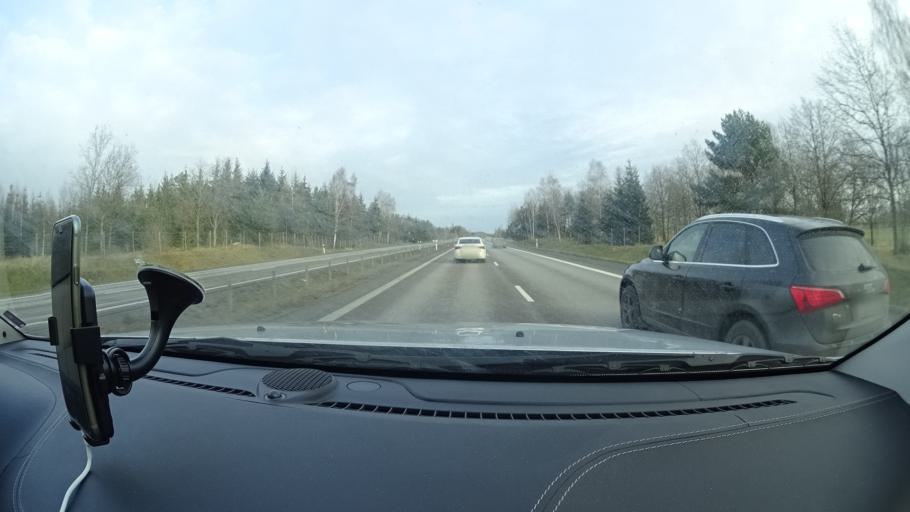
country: SE
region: OEstergoetland
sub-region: Linkopings Kommun
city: Linghem
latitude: 58.4630
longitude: 15.7961
